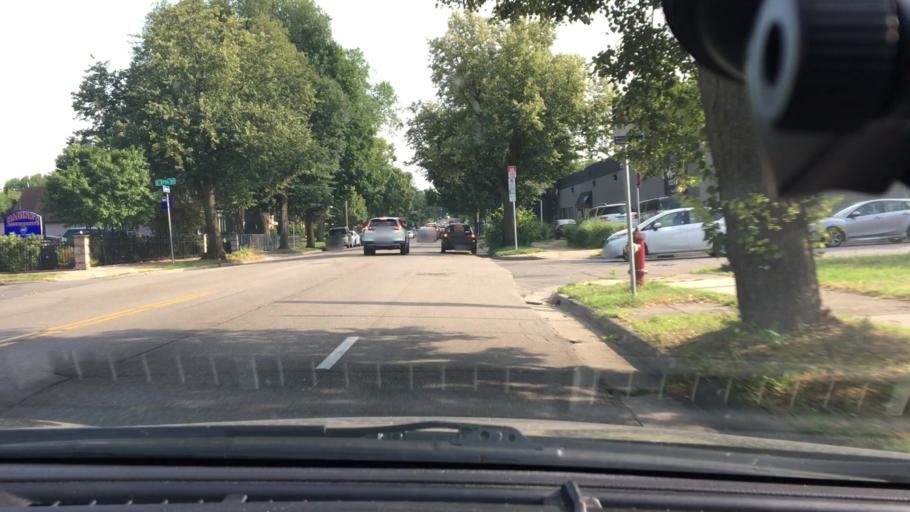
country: US
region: Minnesota
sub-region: Hennepin County
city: Minneapolis
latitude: 44.9361
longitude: -93.2475
